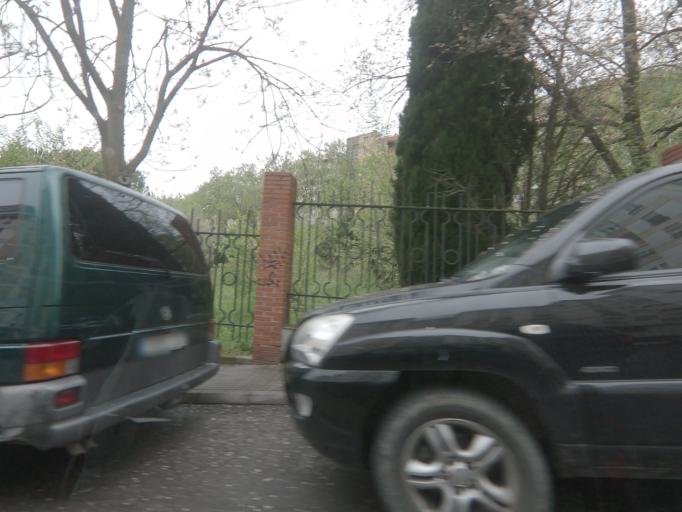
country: ES
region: Extremadura
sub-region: Provincia de Caceres
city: Caceres
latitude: 39.4748
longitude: -6.3796
